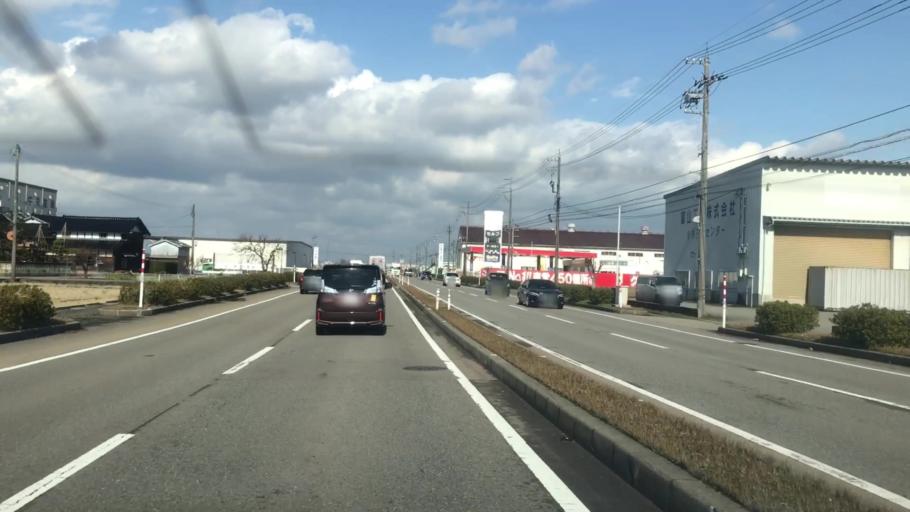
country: JP
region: Toyama
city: Kuragaki-kosugi
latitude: 36.7074
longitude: 137.0794
